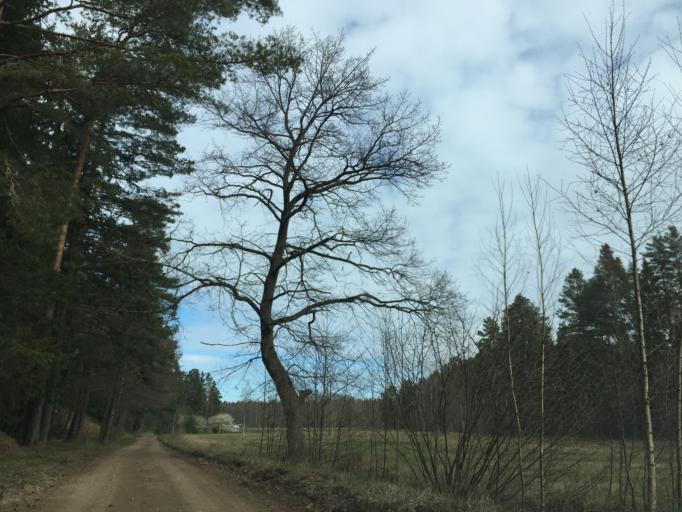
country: LV
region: Salacgrivas
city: Salacgriva
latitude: 57.5303
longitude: 24.3763
